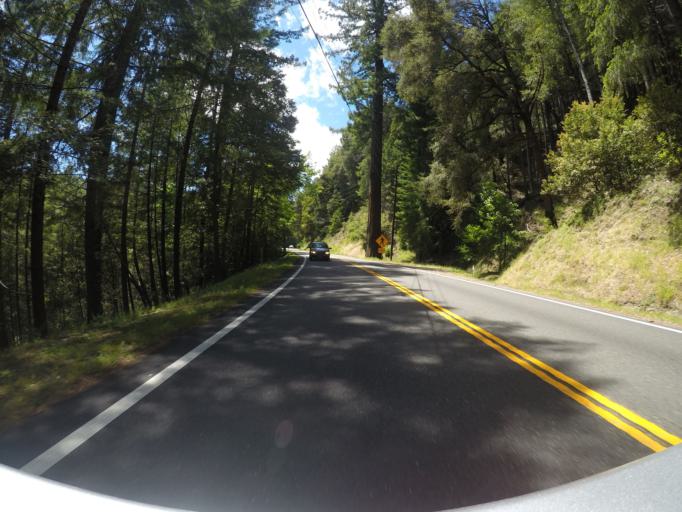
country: US
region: California
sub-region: Humboldt County
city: Redway
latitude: 39.9149
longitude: -123.7614
